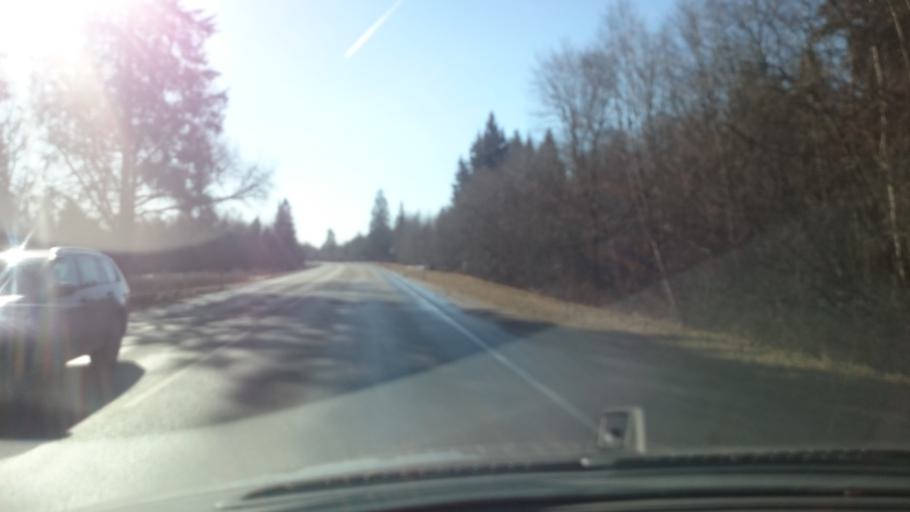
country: EE
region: Raplamaa
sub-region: Kohila vald
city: Kohila
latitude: 59.2462
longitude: 24.7484
